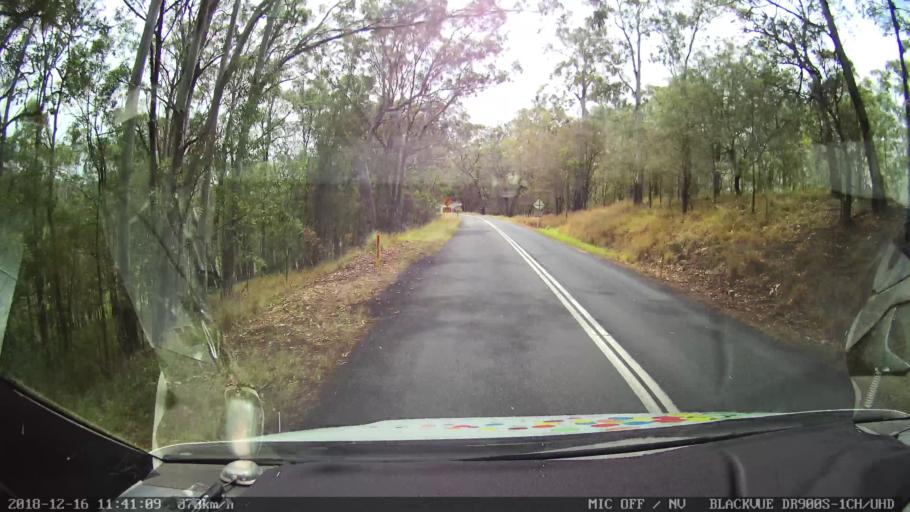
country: AU
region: New South Wales
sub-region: Tenterfield Municipality
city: Carrolls Creek
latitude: -28.9591
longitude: 152.2059
